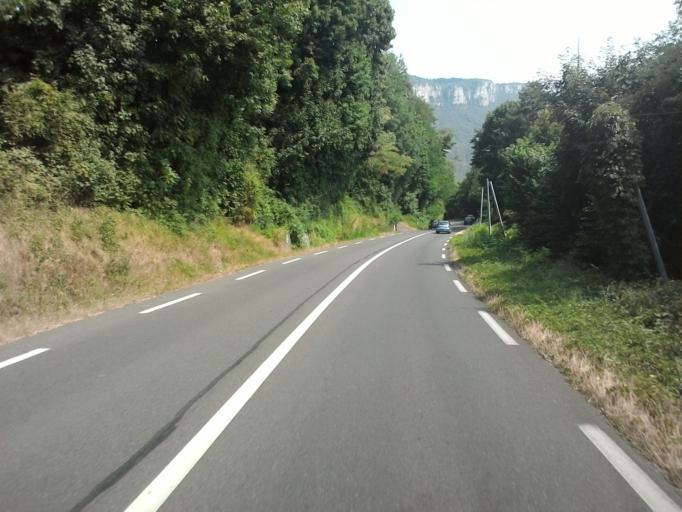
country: FR
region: Rhone-Alpes
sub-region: Departement de l'Isere
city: Coublevie
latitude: 45.3438
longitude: 5.6077
